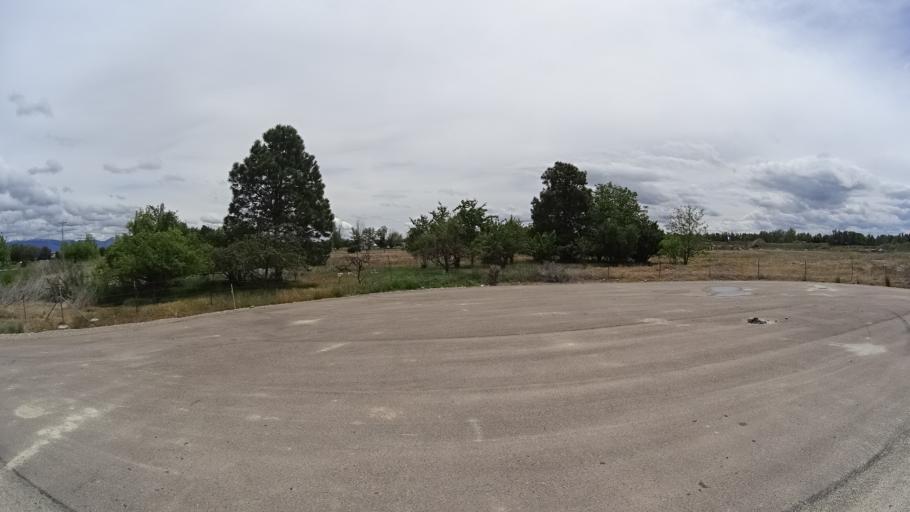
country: US
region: Idaho
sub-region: Ada County
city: Star
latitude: 43.6897
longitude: -116.4590
